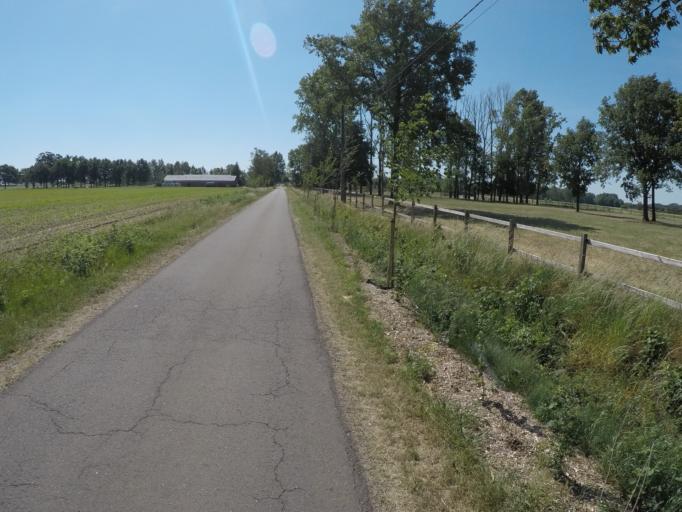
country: BE
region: Flanders
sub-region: Provincie Antwerpen
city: Wuustwezel
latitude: 51.4157
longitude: 4.6316
